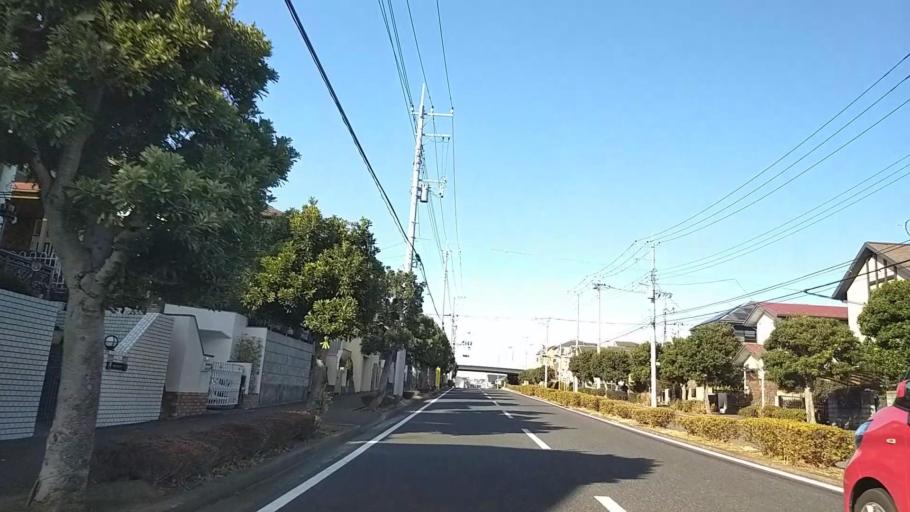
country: JP
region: Kanagawa
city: Atsugi
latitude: 35.4385
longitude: 139.3298
